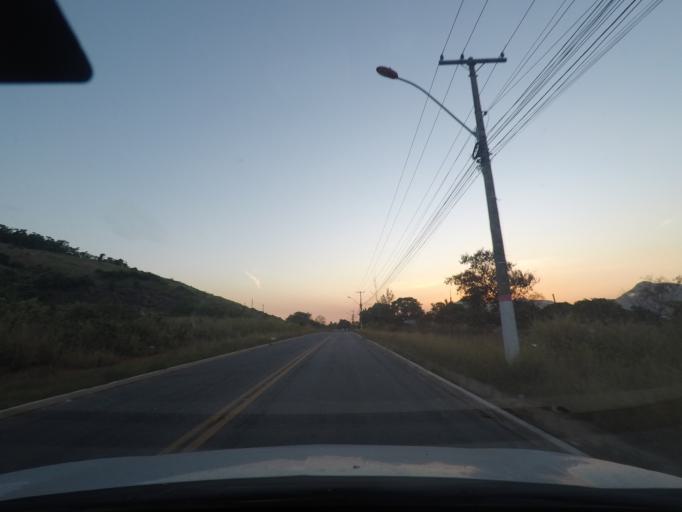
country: BR
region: Rio de Janeiro
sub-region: Niteroi
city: Niteroi
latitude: -22.9542
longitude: -42.9758
